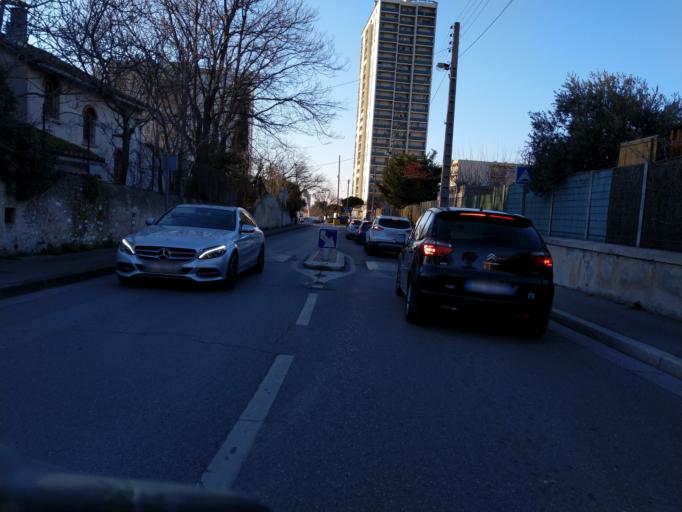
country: FR
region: Provence-Alpes-Cote d'Azur
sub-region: Departement des Bouches-du-Rhone
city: Marseille 10
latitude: 43.2784
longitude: 5.4293
